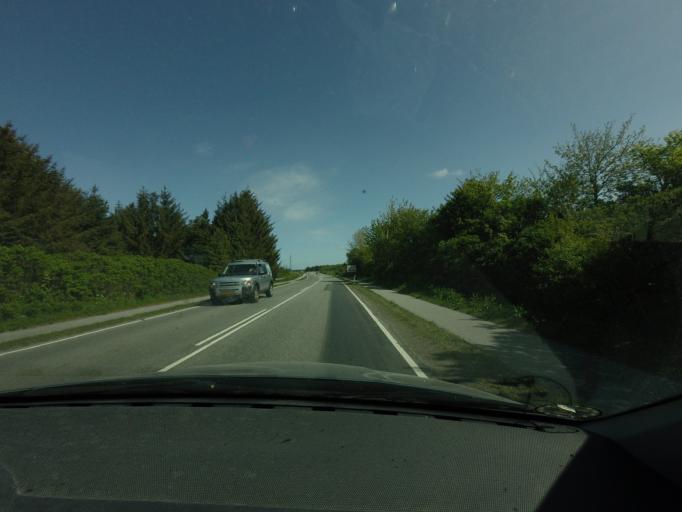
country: DK
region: North Denmark
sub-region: Jammerbugt Kommune
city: Pandrup
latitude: 57.3154
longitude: 9.7080
